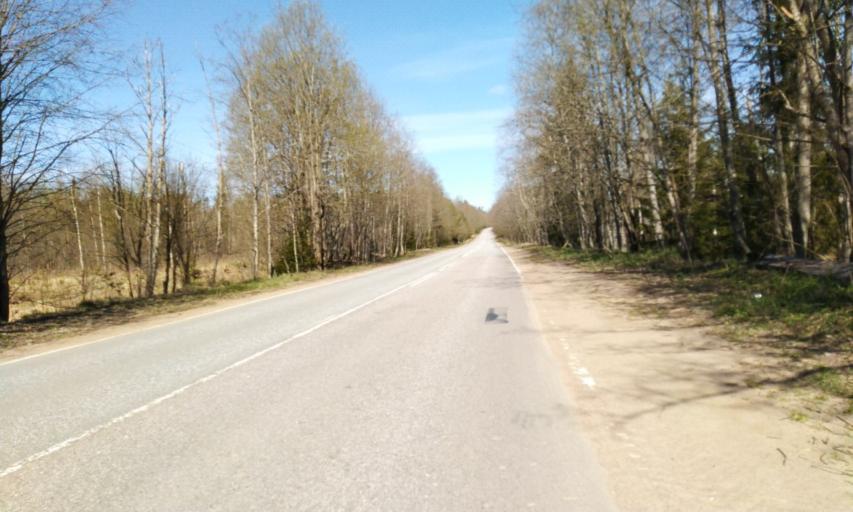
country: RU
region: Leningrad
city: Garbolovo
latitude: 60.4043
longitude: 30.4707
